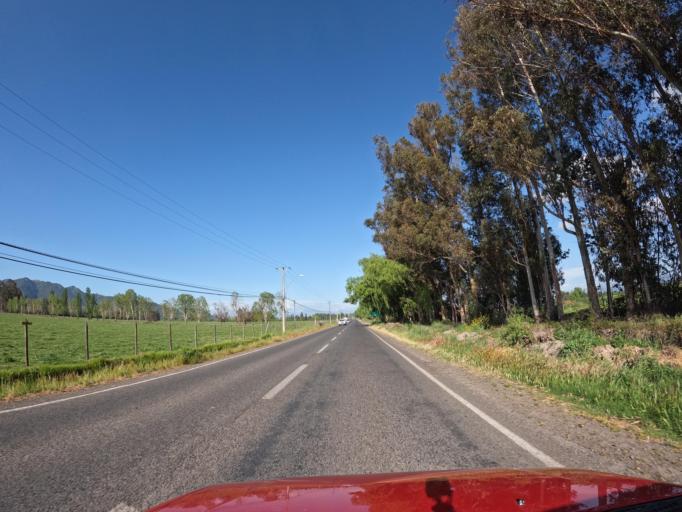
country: CL
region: Maule
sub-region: Provincia de Curico
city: Rauco
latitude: -34.8684
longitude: -71.2569
